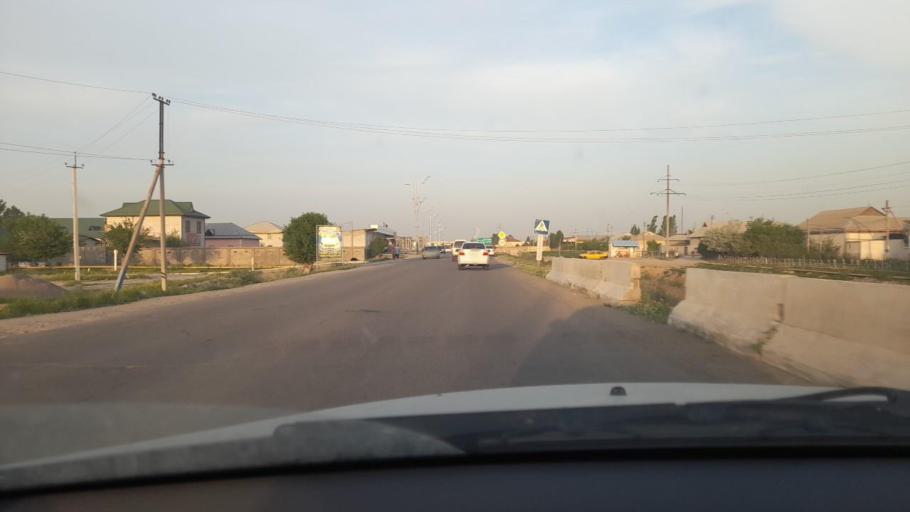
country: UZ
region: Sirdaryo
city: Guliston
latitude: 40.5072
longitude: 68.7478
